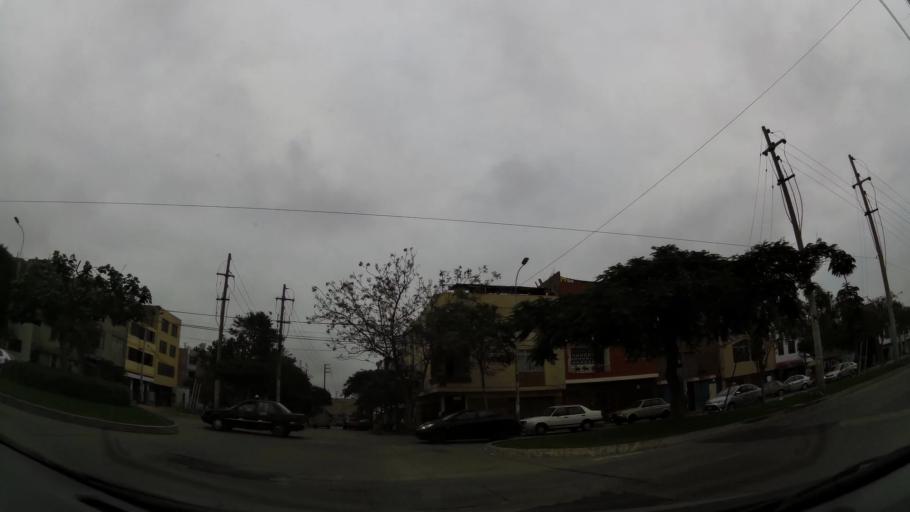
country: PE
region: Lima
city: Lima
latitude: -12.0626
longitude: -77.0633
